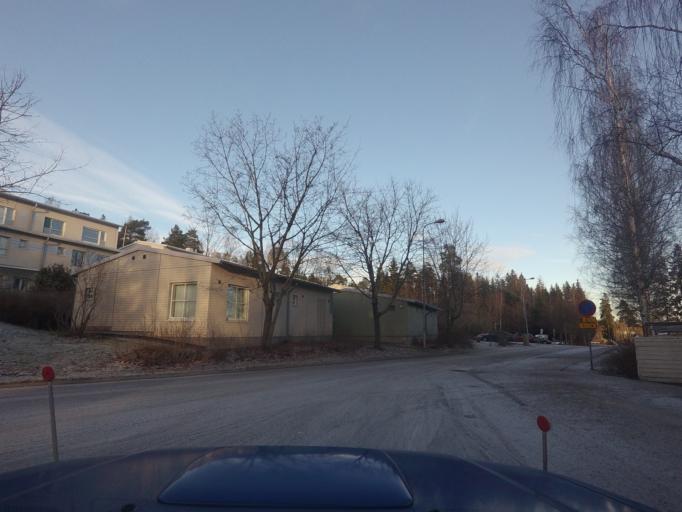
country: FI
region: Uusimaa
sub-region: Helsinki
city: Espoo
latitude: 60.2067
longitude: 24.6341
